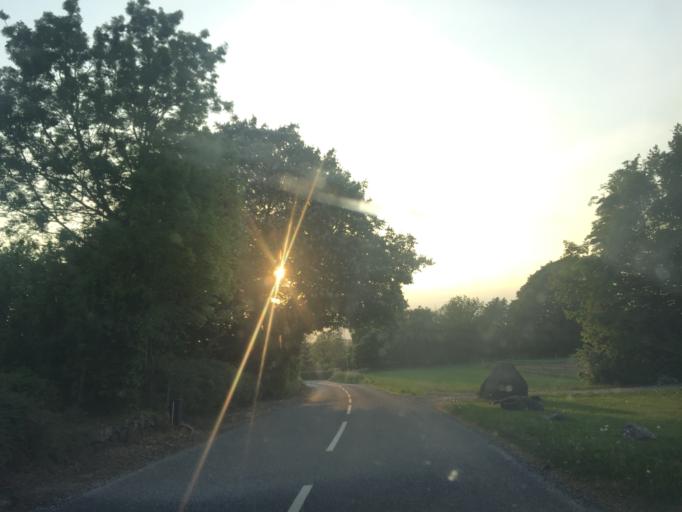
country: DK
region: South Denmark
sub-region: Odense Kommune
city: Bellinge
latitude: 55.3815
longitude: 10.3071
